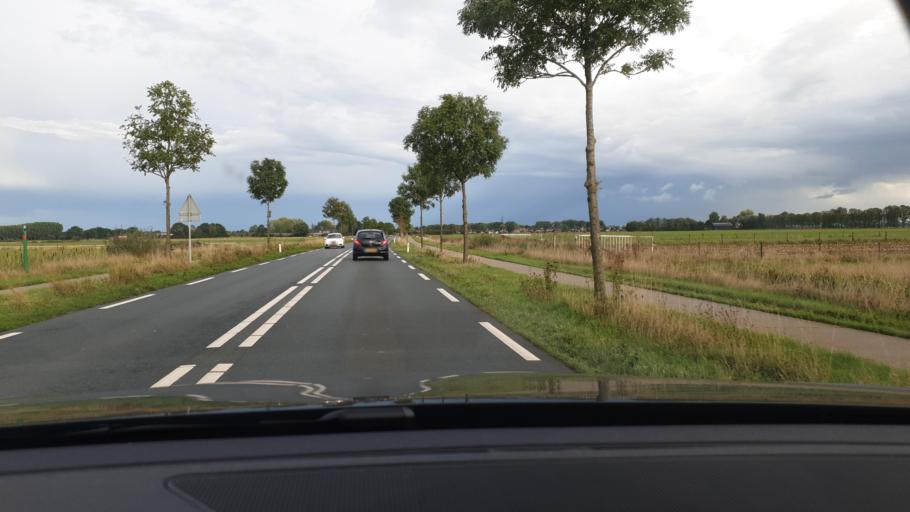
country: NL
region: North Brabant
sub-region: Gemeente Oss
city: Berghem
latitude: 51.8024
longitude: 5.5632
